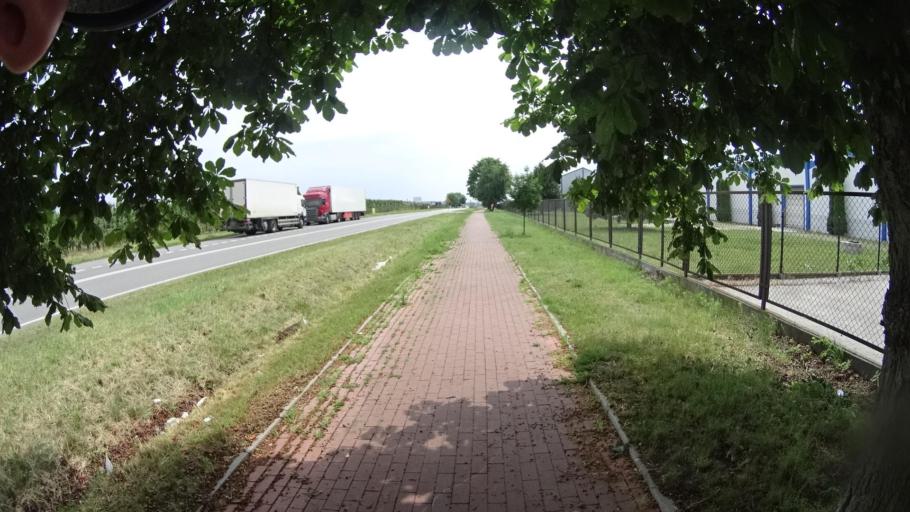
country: PL
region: Masovian Voivodeship
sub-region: Powiat grojecki
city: Grojec
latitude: 51.8852
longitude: 20.8631
